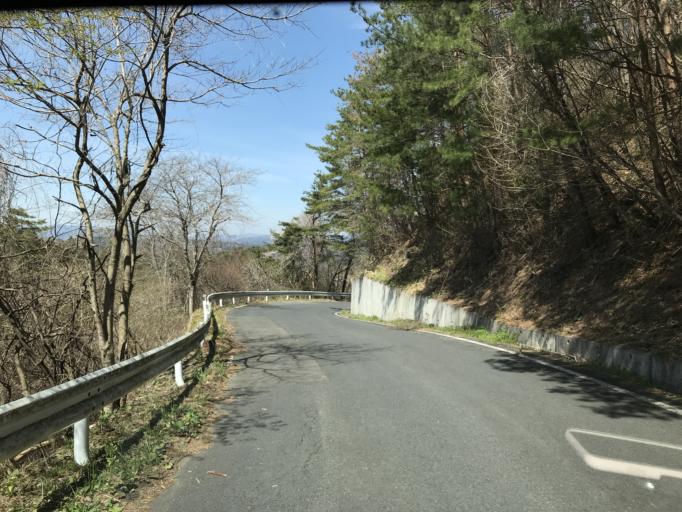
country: JP
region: Iwate
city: Ichinoseki
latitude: 38.8322
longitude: 141.2838
